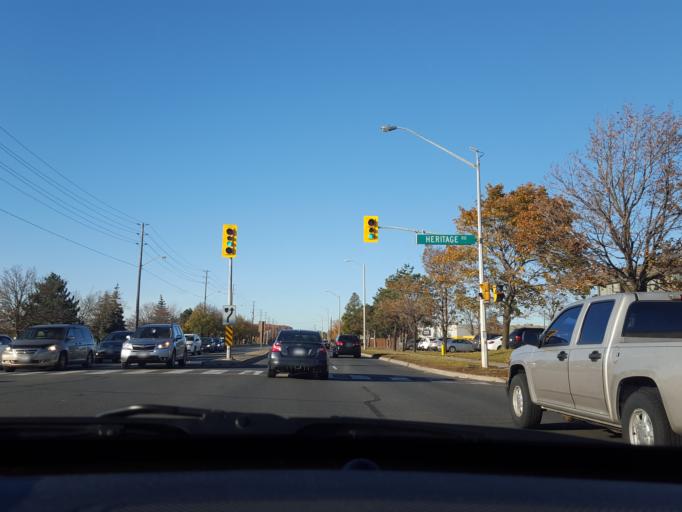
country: CA
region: Ontario
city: Markham
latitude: 43.8698
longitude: -79.2851
